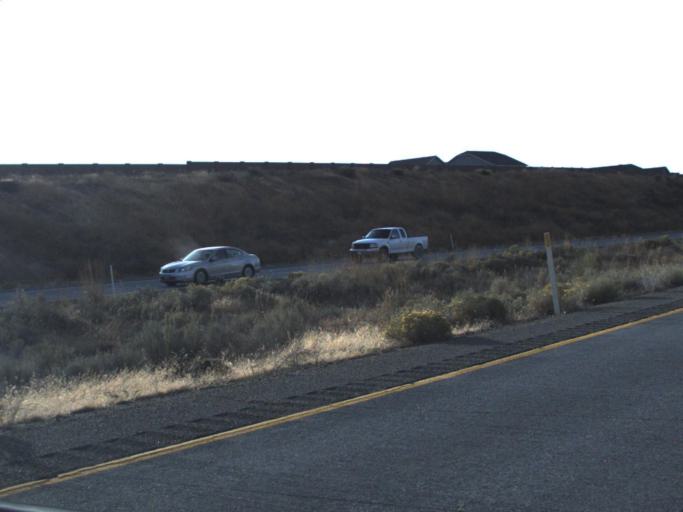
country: US
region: Washington
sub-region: Benton County
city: Richland
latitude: 46.2078
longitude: -119.3393
